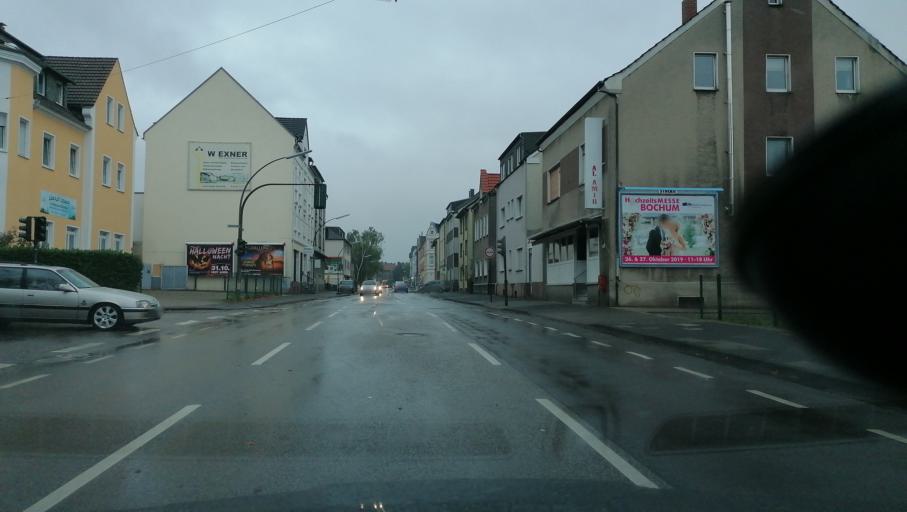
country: DE
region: North Rhine-Westphalia
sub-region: Regierungsbezirk Munster
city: Recklinghausen
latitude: 51.5760
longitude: 7.2005
